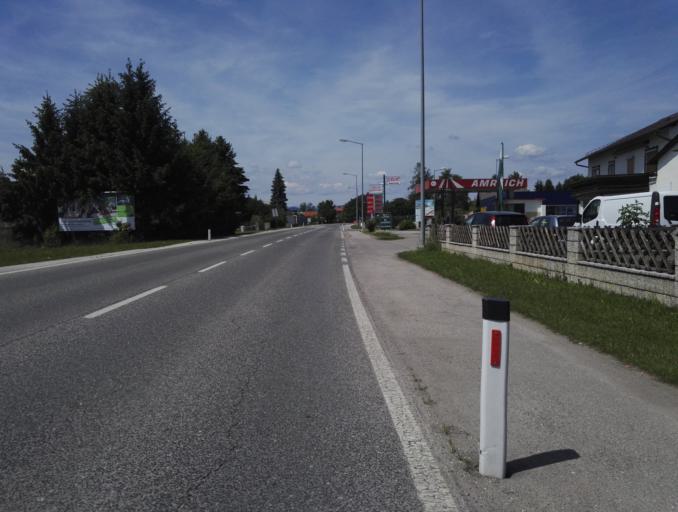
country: AT
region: Styria
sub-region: Politischer Bezirk Graz-Umgebung
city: Gossendorf
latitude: 46.9863
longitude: 15.4592
